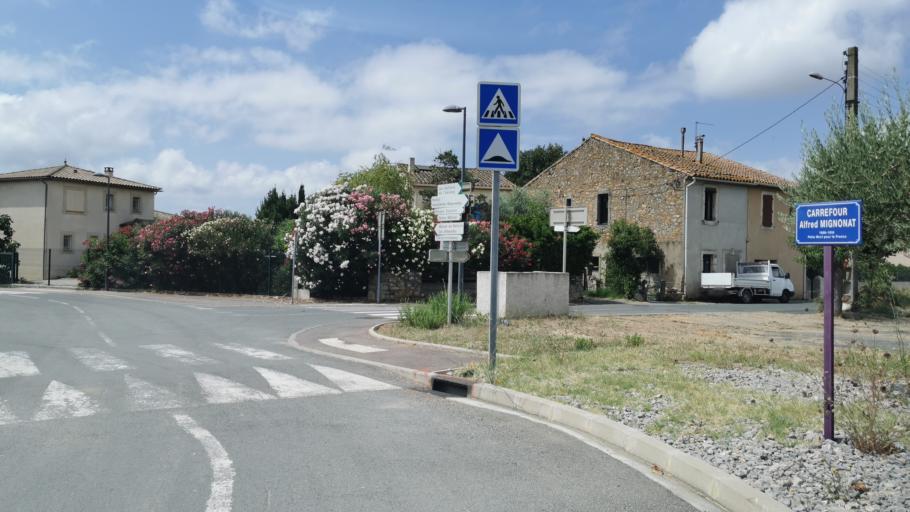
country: FR
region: Languedoc-Roussillon
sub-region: Departement de l'Aude
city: Bizanet
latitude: 43.1656
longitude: 2.8673
